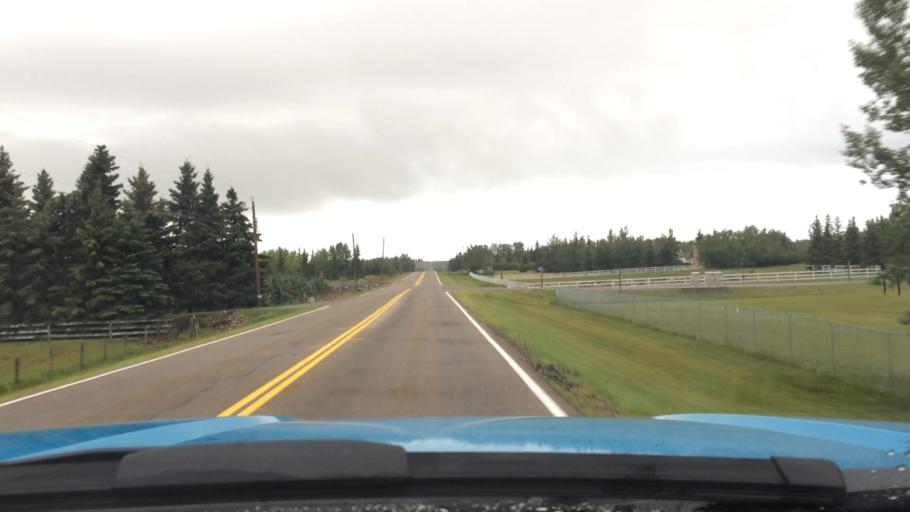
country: CA
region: Alberta
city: Airdrie
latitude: 51.2001
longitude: -114.1412
